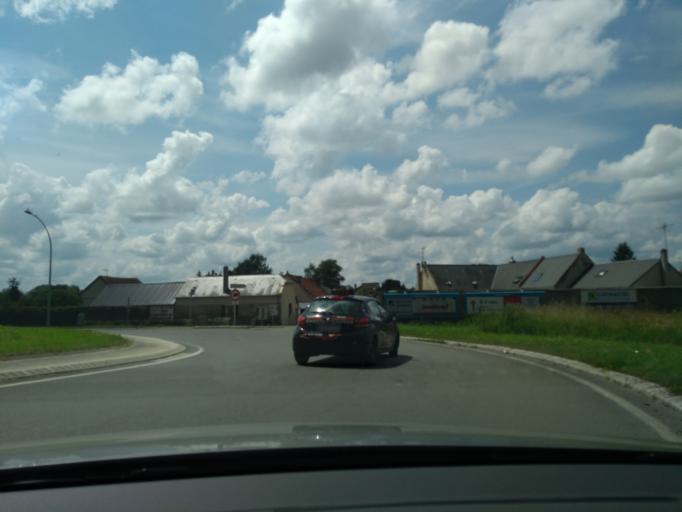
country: FR
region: Picardie
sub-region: Departement de l'Aisne
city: Athies-sous-Laon
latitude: 49.5944
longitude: 3.6595
